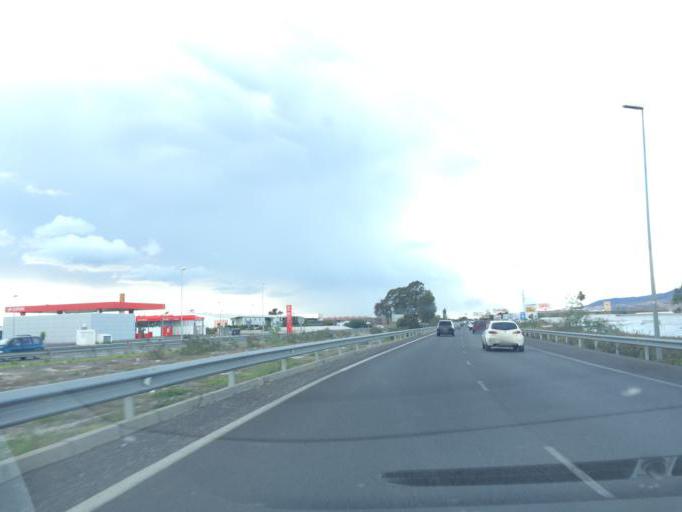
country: ES
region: Andalusia
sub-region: Provincia de Almeria
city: Almeria
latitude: 36.8440
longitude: -2.4222
